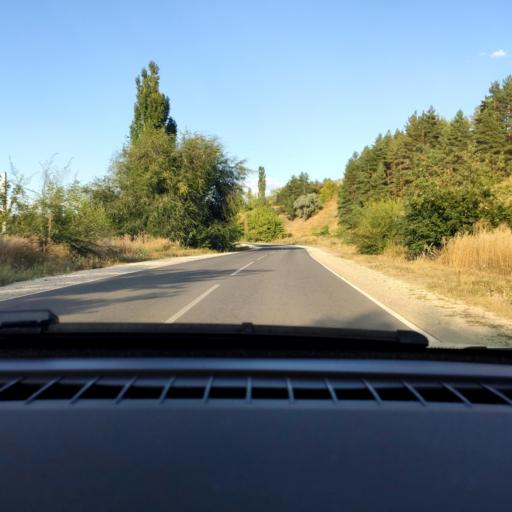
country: RU
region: Voronezj
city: Semiluki
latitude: 51.6672
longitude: 39.0187
